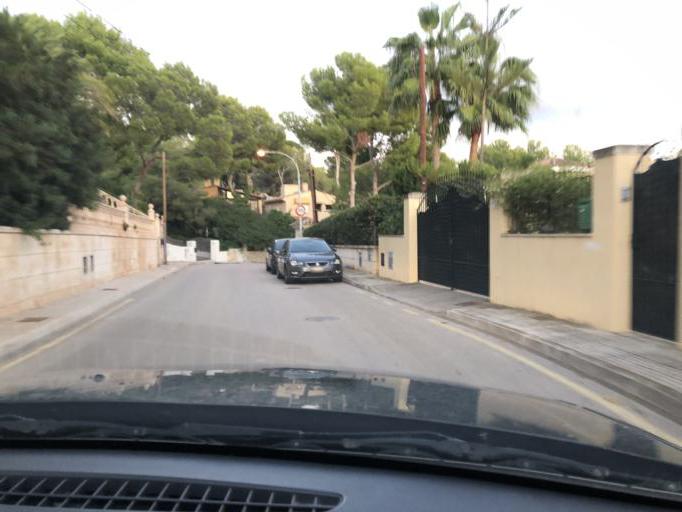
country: ES
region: Balearic Islands
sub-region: Illes Balears
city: Santa Ponsa
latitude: 39.5280
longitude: 2.4769
